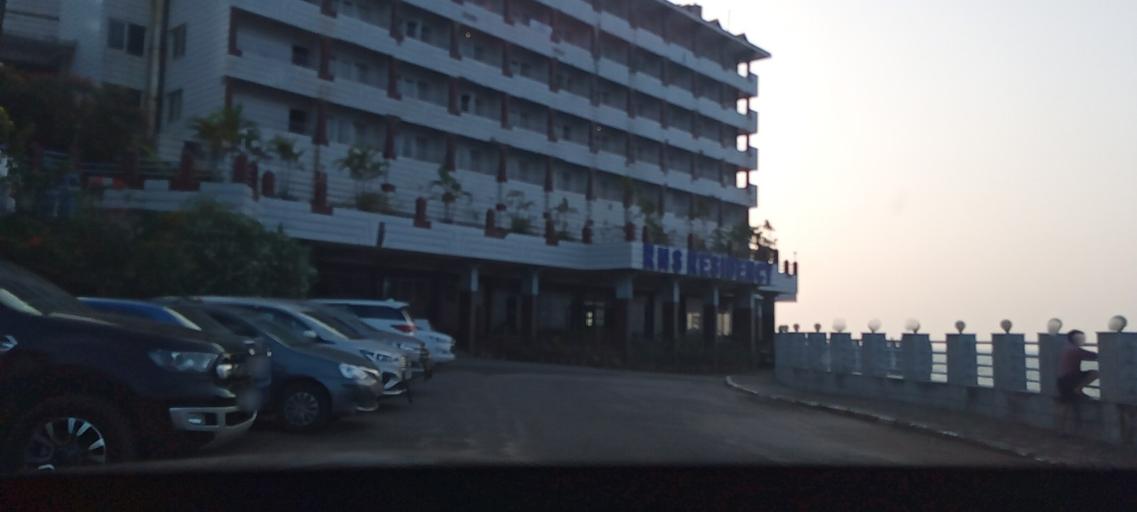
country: IN
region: Karnataka
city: Murudeshwara
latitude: 14.0951
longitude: 74.4838
